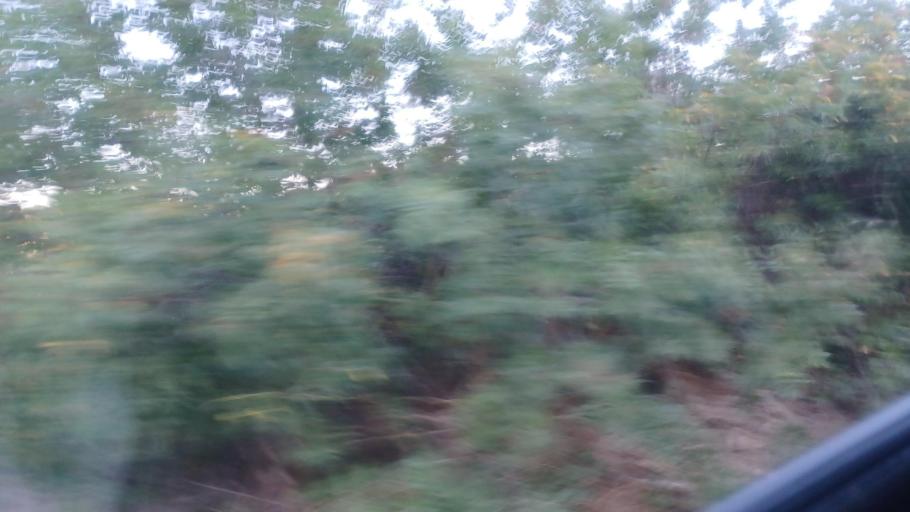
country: CY
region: Pafos
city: Tala
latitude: 34.8620
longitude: 32.4680
